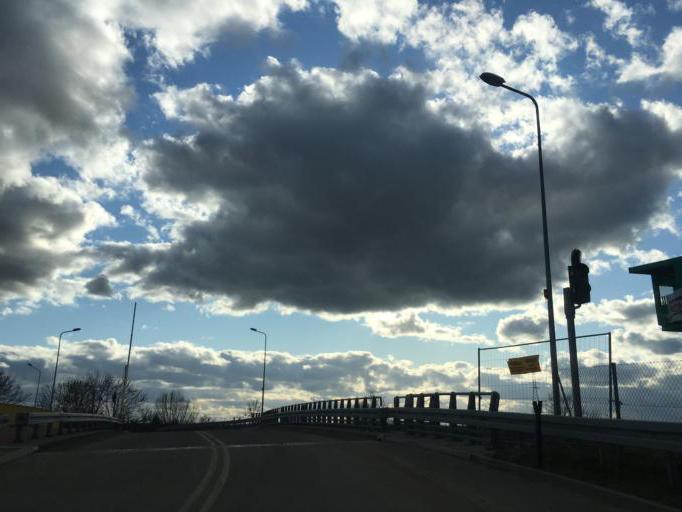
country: PL
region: Pomeranian Voivodeship
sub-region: Powiat gdanski
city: Cedry Wielkie
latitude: 54.3090
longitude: 18.9236
